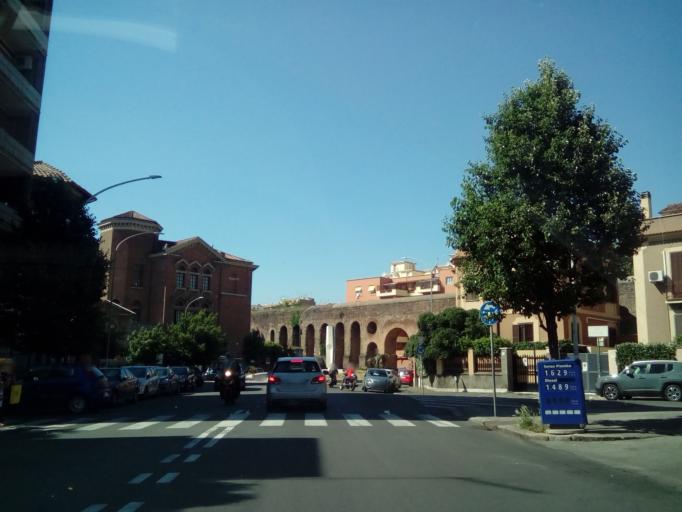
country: IT
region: Latium
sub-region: Citta metropolitana di Roma Capitale
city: Rome
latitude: 41.8865
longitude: 12.5215
